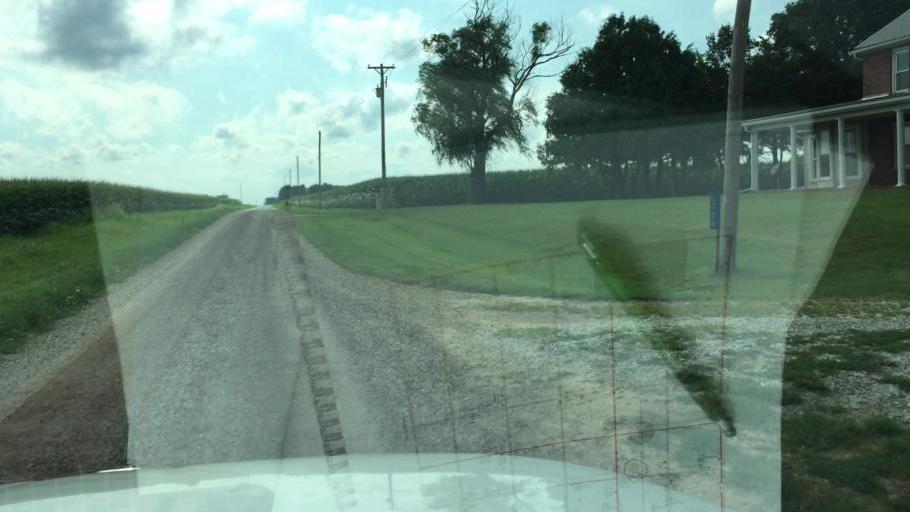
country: US
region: Illinois
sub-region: Hancock County
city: Carthage
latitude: 40.5356
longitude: -91.1723
